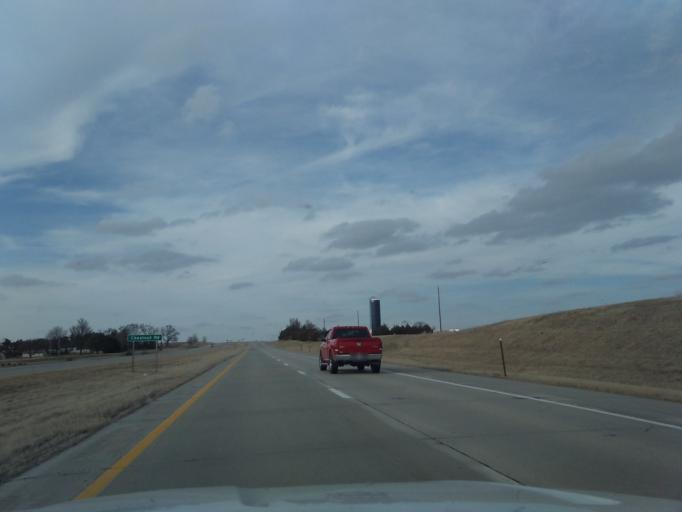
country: US
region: Nebraska
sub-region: Gage County
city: Beatrice
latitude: 40.3902
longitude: -96.7425
